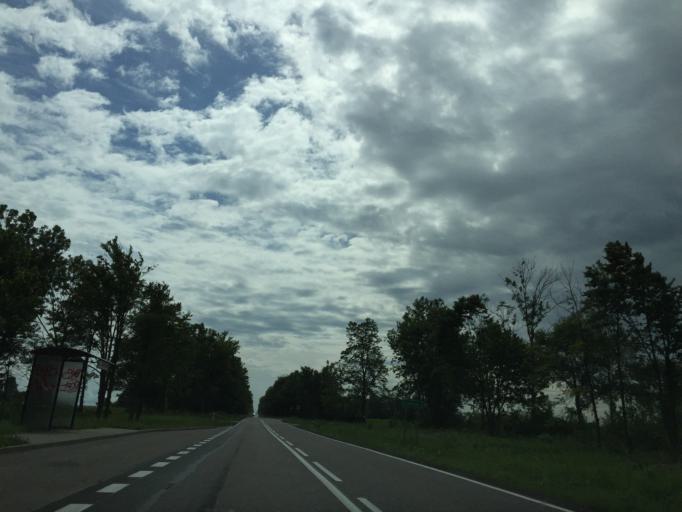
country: PL
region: Podlasie
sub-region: Powiat bielski
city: Bocki
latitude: 52.6226
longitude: 23.0031
